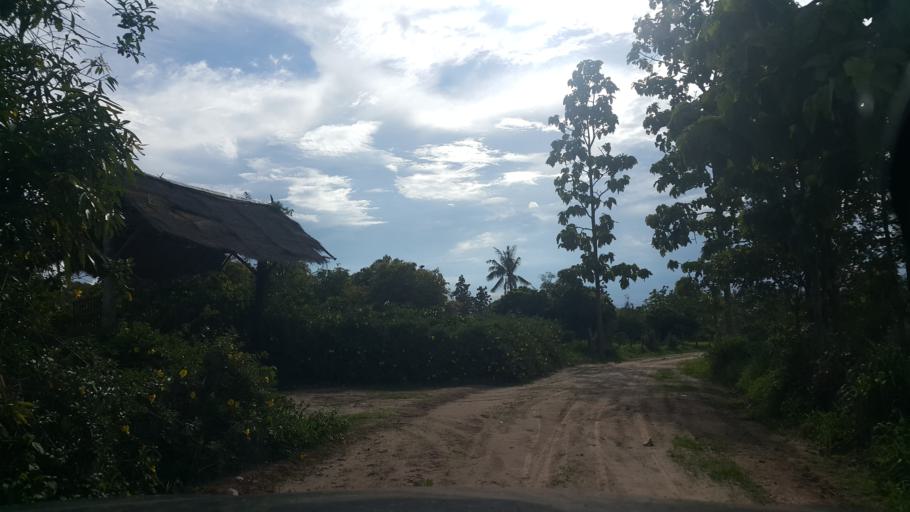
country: TH
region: Chiang Mai
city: Mae On
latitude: 18.7110
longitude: 99.2154
